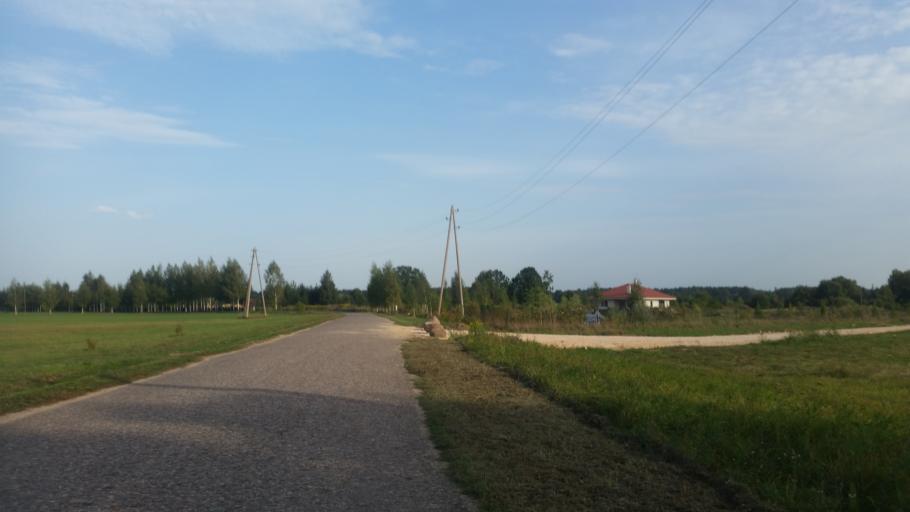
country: LV
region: Ikskile
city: Ikskile
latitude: 56.8178
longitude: 24.5416
